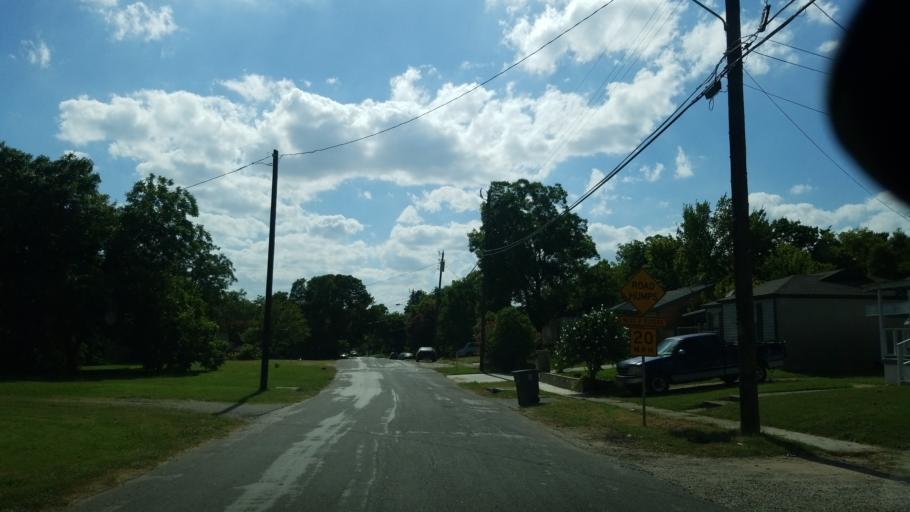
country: US
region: Texas
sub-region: Dallas County
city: Balch Springs
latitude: 32.7715
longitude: -96.7054
